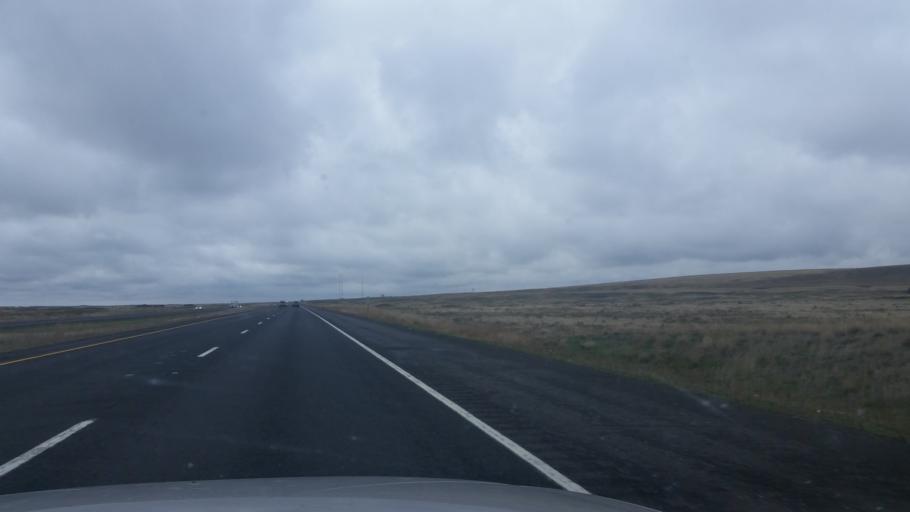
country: US
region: Washington
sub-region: Spokane County
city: Medical Lake
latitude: 47.3313
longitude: -117.9233
